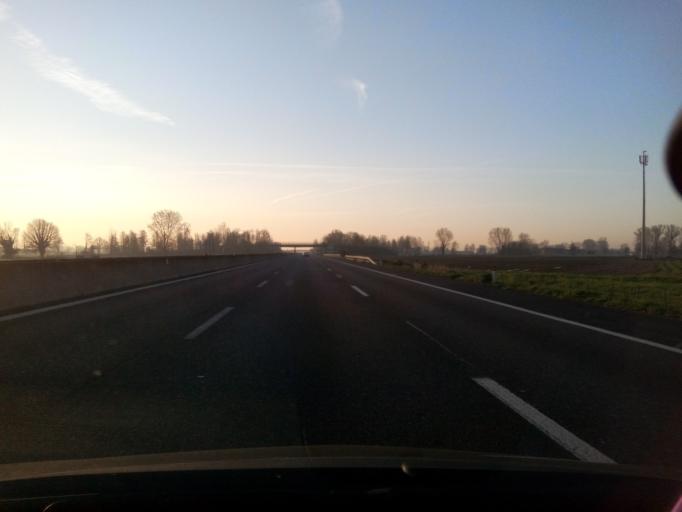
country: IT
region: Lombardy
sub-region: Citta metropolitana di Milano
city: San Zenone al Lambro
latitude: 45.3270
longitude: 9.3673
